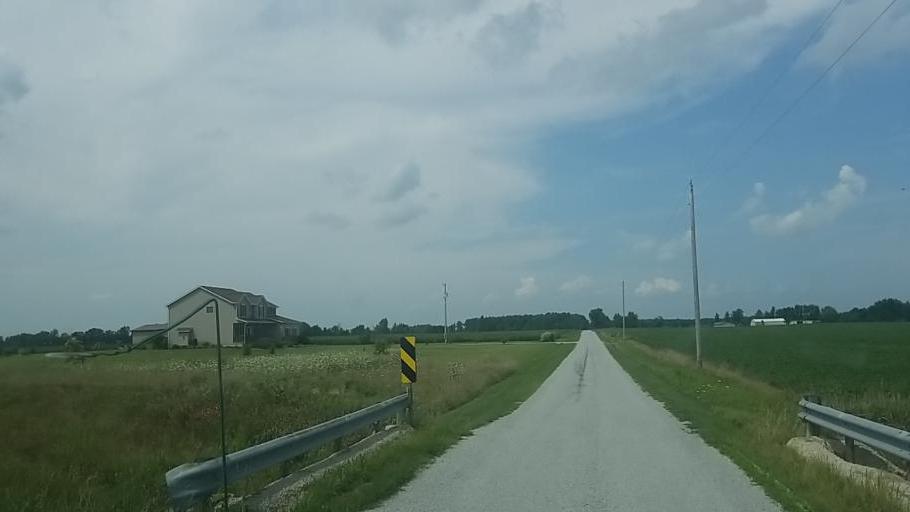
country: US
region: Ohio
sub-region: Hardin County
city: Forest
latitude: 40.7682
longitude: -83.5955
